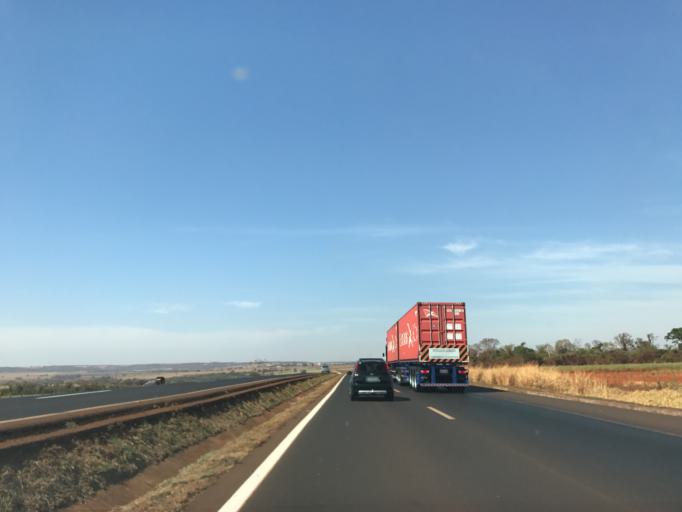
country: BR
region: Minas Gerais
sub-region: Centralina
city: Centralina
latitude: -18.5217
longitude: -49.1905
